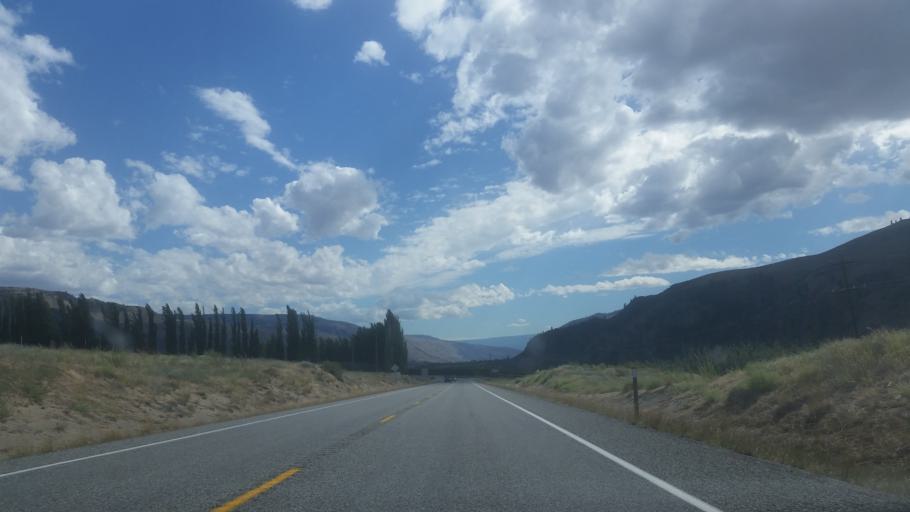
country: US
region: Washington
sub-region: Chelan County
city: Entiat
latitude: 47.7206
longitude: -120.2019
